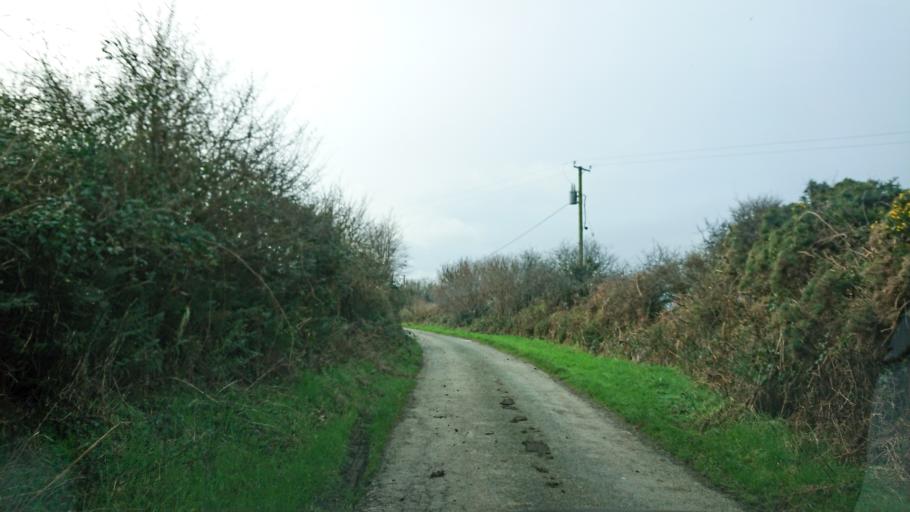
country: IE
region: Munster
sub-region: Waterford
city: Tra Mhor
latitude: 52.1978
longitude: -7.1685
